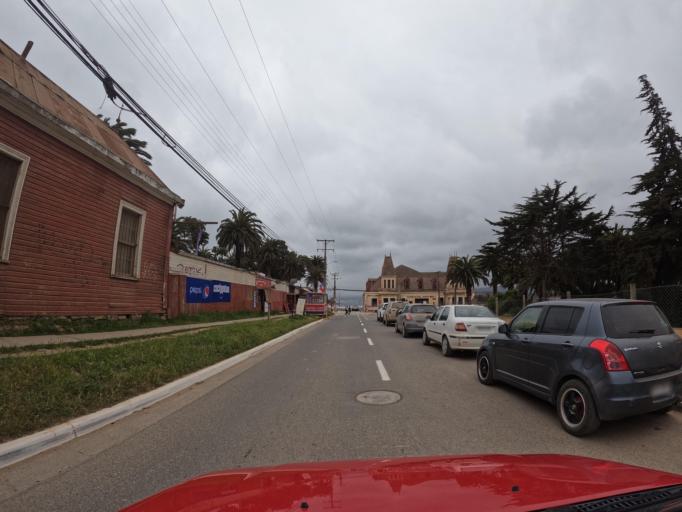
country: CL
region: O'Higgins
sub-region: Provincia de Colchagua
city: Santa Cruz
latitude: -34.3872
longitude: -72.0103
